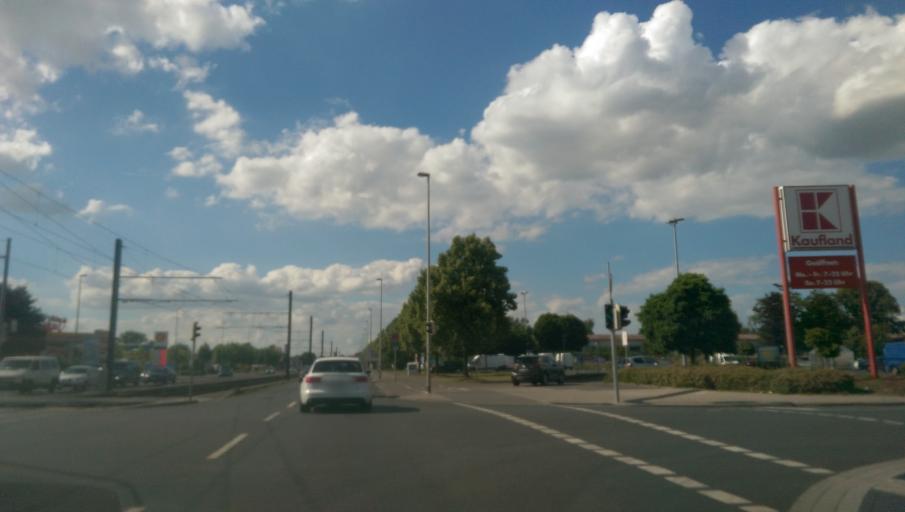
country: DE
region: Lower Saxony
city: Hannover
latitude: 52.4079
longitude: 9.7096
